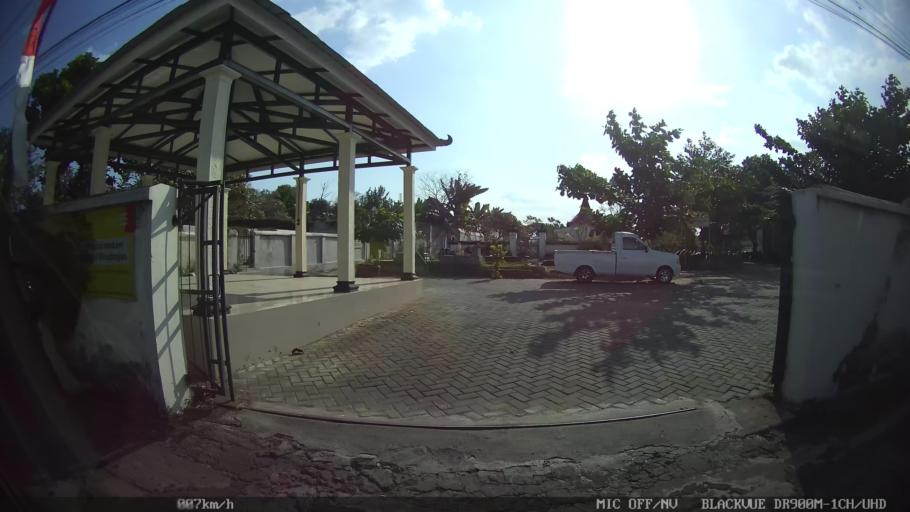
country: ID
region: Daerah Istimewa Yogyakarta
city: Yogyakarta
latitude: -7.7959
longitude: 110.3508
